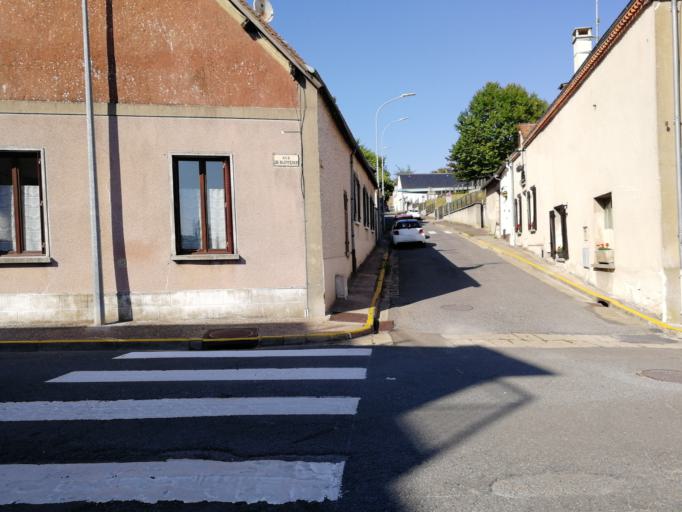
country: FR
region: Centre
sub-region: Departement d'Eure-et-Loir
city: Gallardon
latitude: 48.5252
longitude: 1.6858
